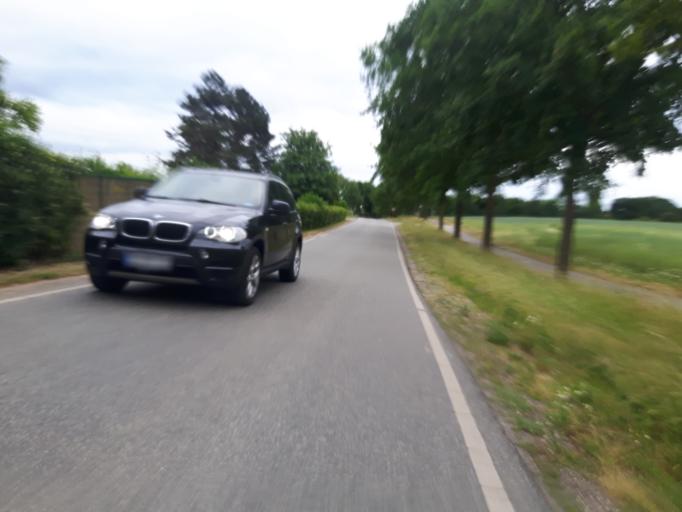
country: DE
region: Schleswig-Holstein
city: Schashagen
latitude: 54.1041
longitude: 10.8954
